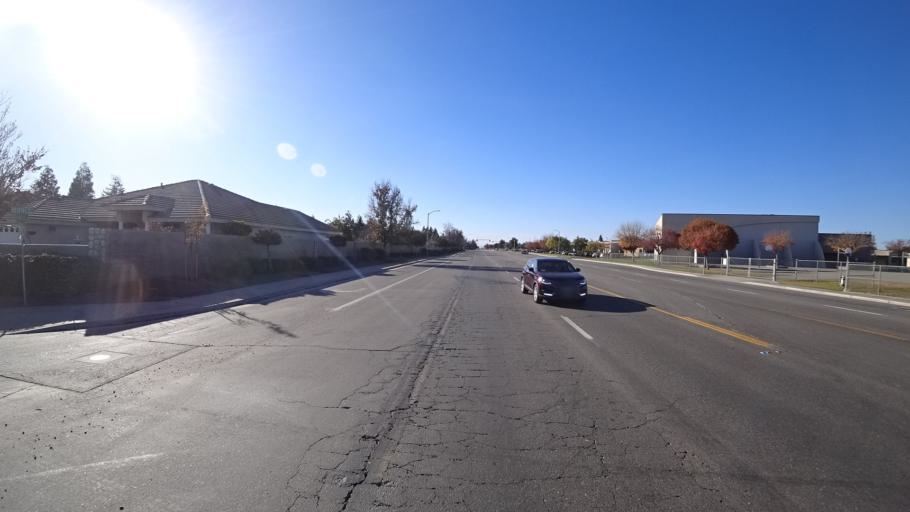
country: US
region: California
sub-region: Kern County
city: Greenfield
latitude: 35.2813
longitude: -119.0452
